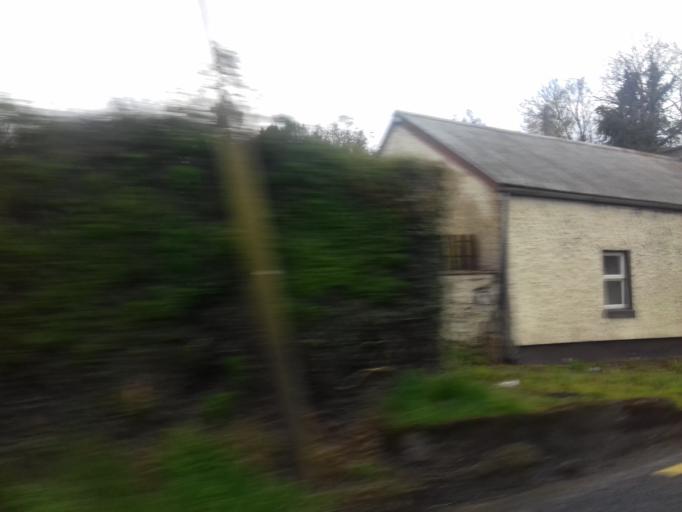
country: IE
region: Ulster
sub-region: An Cabhan
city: Belturbet
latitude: 54.0864
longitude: -7.5104
